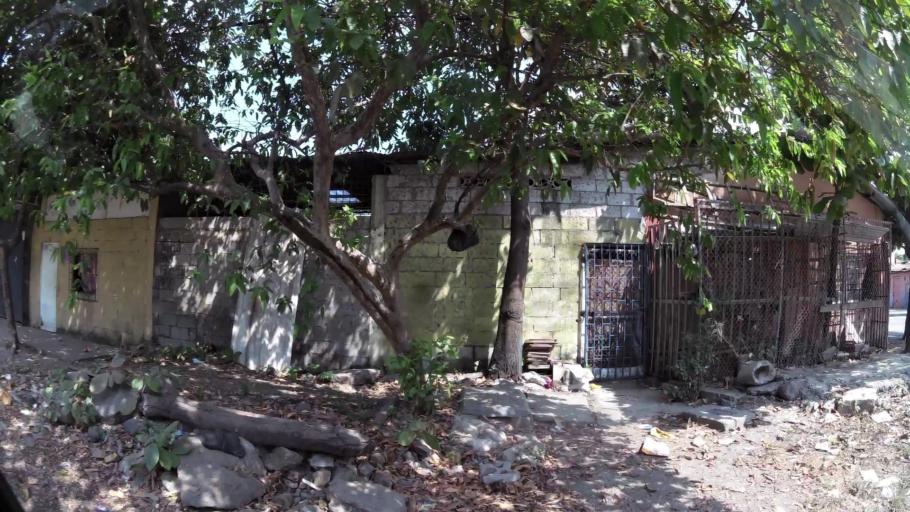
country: EC
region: Guayas
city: Guayaquil
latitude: -2.2668
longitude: -79.8827
